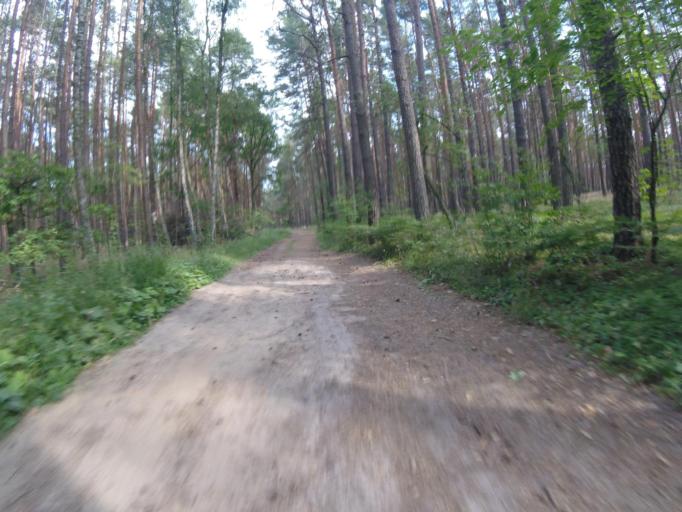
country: DE
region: Brandenburg
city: Wildau
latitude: 52.3193
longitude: 13.7262
